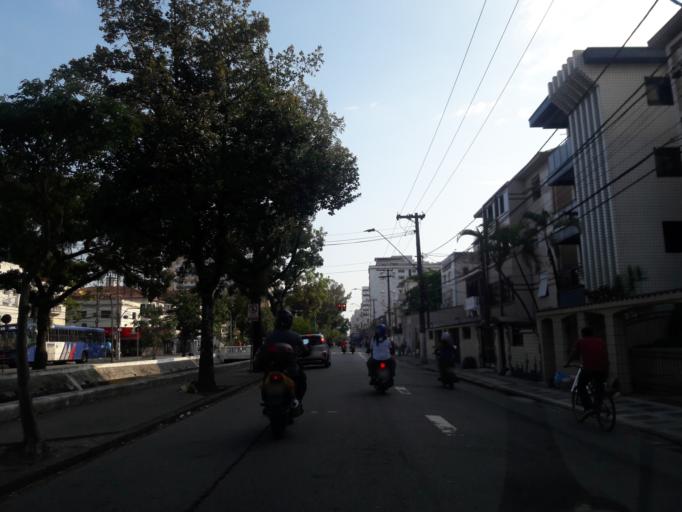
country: BR
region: Sao Paulo
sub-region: Santos
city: Santos
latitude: -23.9564
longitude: -46.3378
